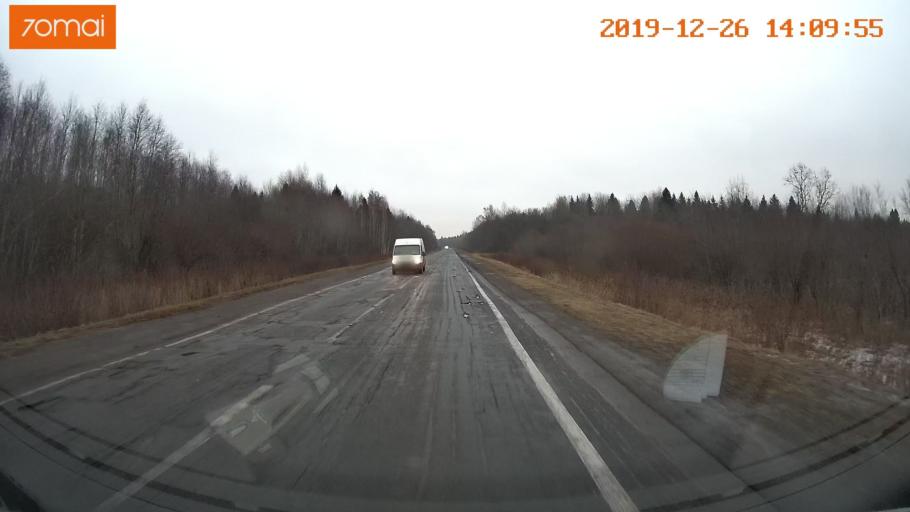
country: RU
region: Jaroslavl
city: Poshekhon'ye
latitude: 58.5085
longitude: 38.9428
